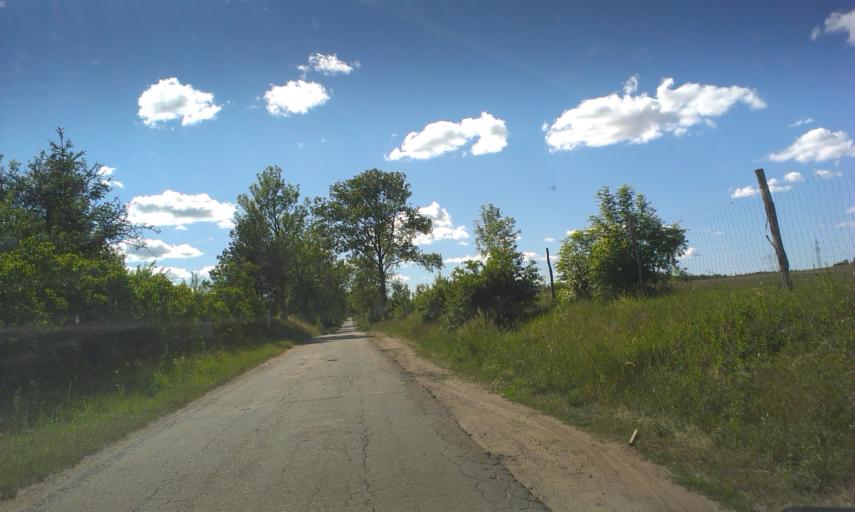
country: PL
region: West Pomeranian Voivodeship
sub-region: Powiat szczecinecki
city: Szczecinek
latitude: 53.8019
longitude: 16.6589
